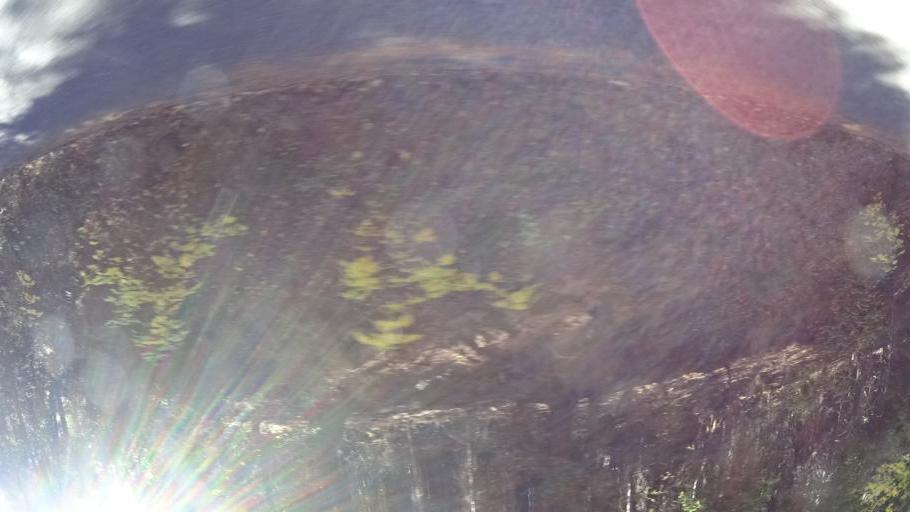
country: US
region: California
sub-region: Siskiyou County
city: Happy Camp
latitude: 41.3501
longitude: -123.0401
